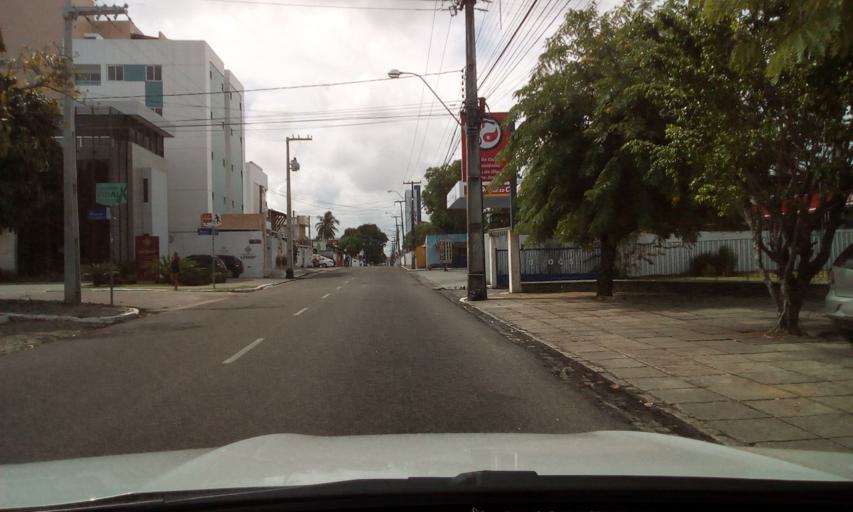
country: BR
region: Paraiba
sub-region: Joao Pessoa
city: Joao Pessoa
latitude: -7.1143
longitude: -34.8611
